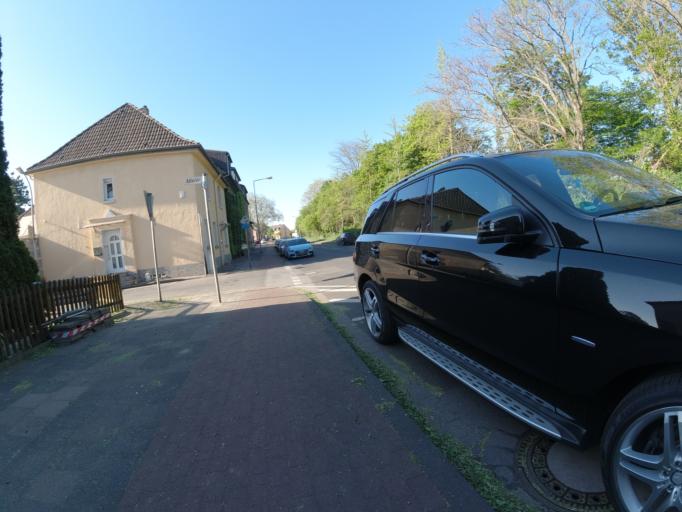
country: DE
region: North Rhine-Westphalia
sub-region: Regierungsbezirk Dusseldorf
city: Hochfeld
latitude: 51.3849
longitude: 6.7113
